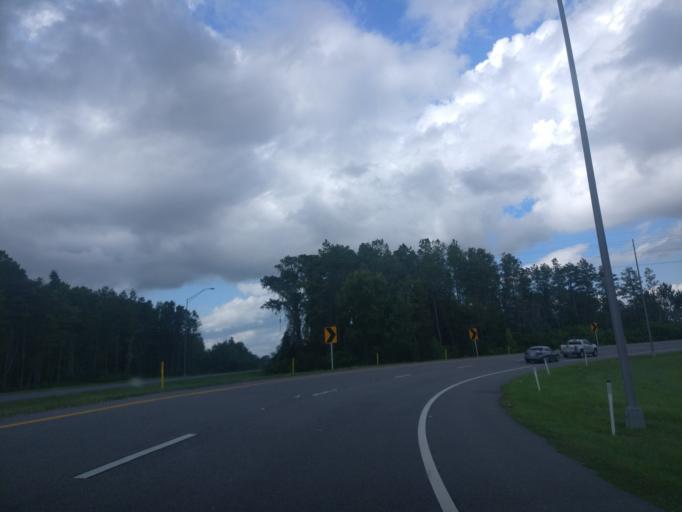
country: US
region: Florida
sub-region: Orange County
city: Hunters Creek
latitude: 28.3721
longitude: -81.4076
